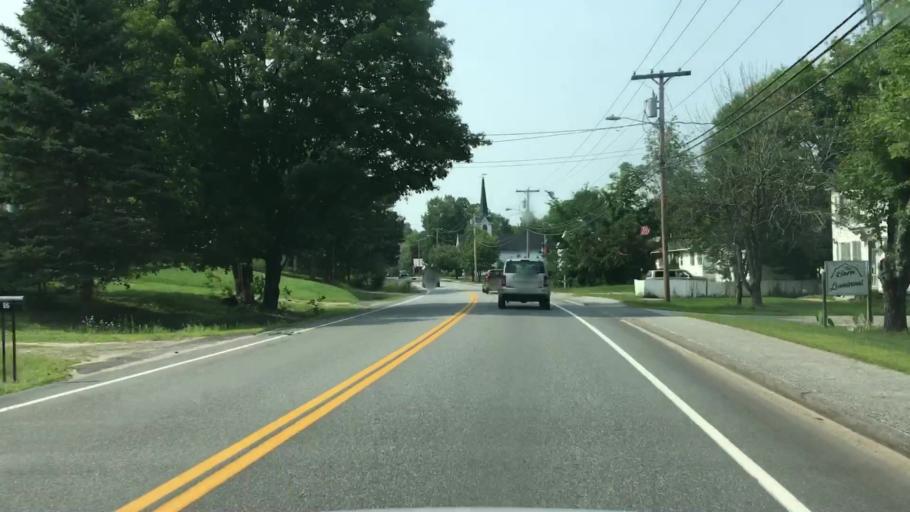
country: US
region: Maine
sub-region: Oxford County
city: Buckfield
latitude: 44.2875
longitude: -70.3610
